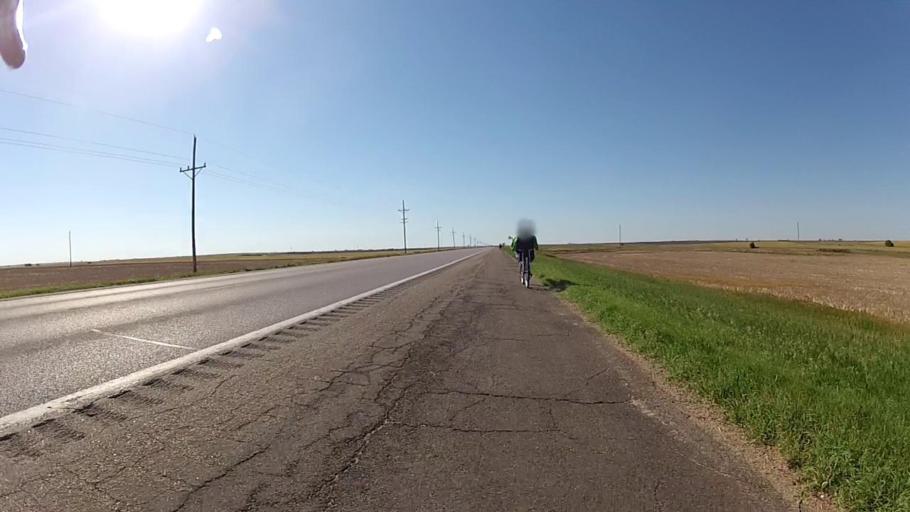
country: US
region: Kansas
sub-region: Ford County
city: Dodge City
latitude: 37.6070
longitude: -99.7094
